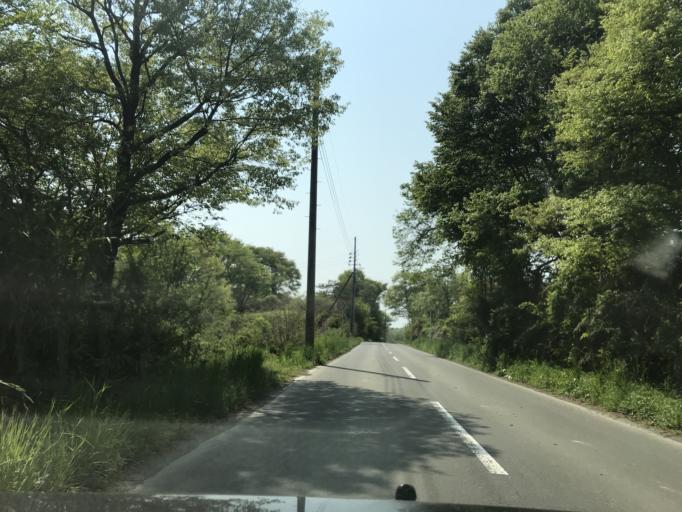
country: JP
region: Iwate
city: Ichinoseki
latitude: 38.8529
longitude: 141.0550
